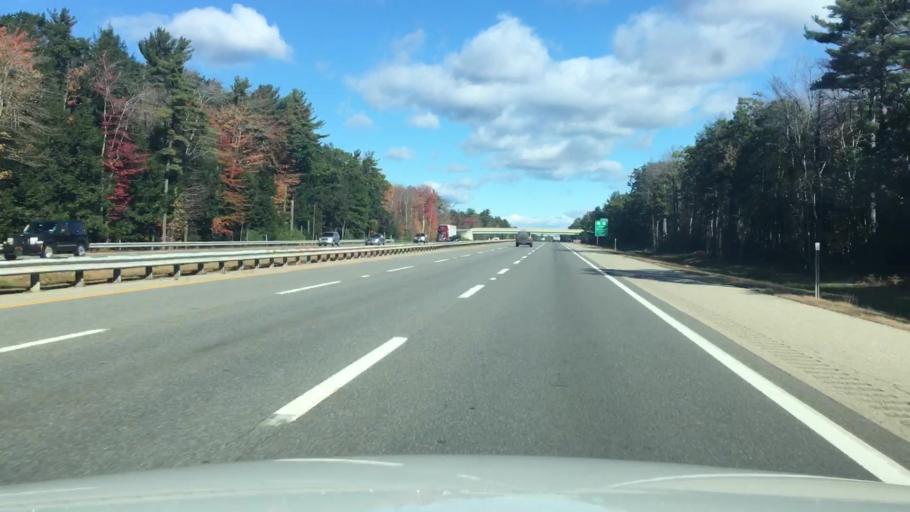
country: US
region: Maine
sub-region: York County
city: Wells Beach Station
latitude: 43.2936
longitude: -70.6162
